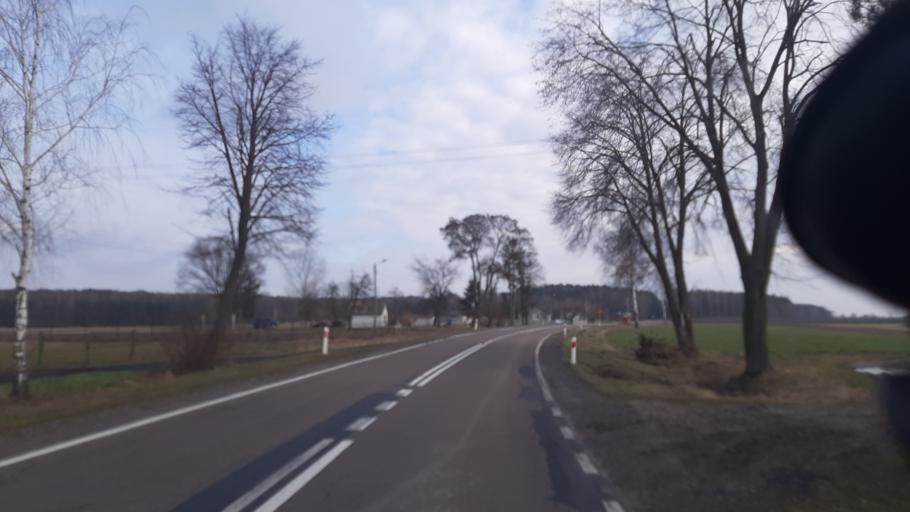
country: PL
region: Lublin Voivodeship
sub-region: Powiat lubartowski
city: Ostrow Lubelski
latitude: 51.4919
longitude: 22.7858
